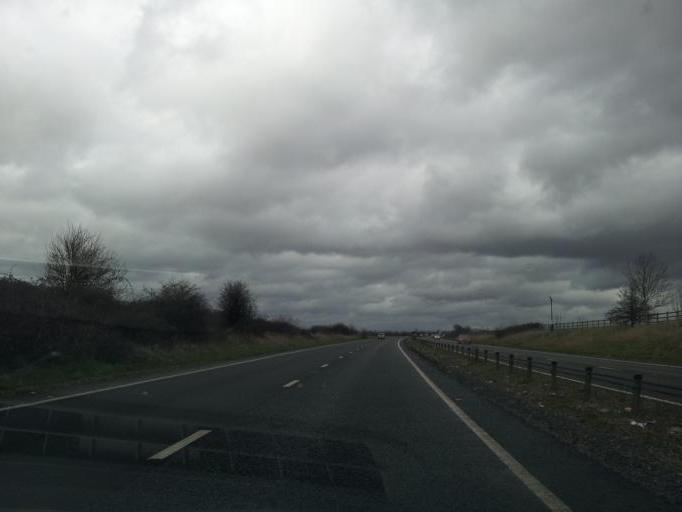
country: GB
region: England
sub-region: Somerset
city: Ilchester
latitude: 51.0152
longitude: -2.6821
